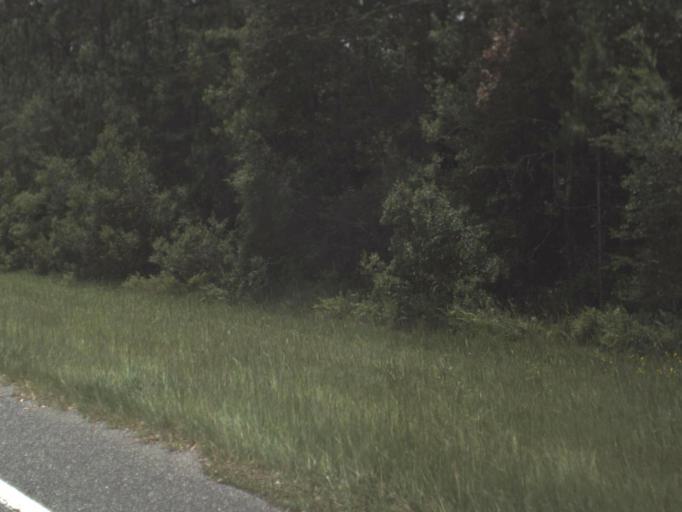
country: US
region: Florida
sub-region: Bradford County
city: Starke
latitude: 29.9756
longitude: -82.2231
